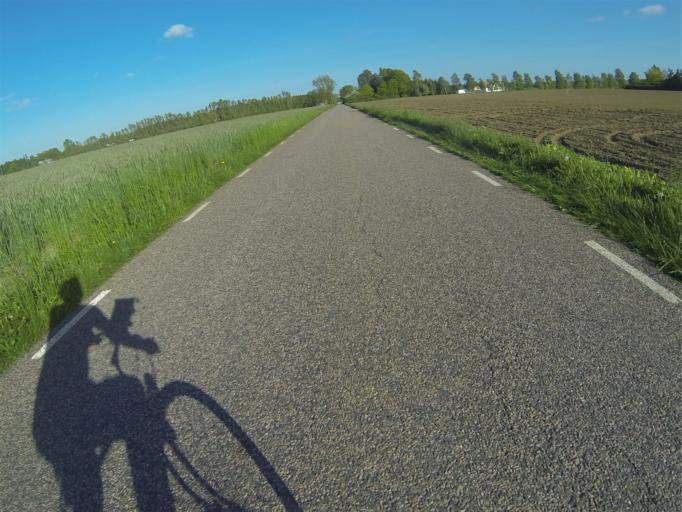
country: SE
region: Skane
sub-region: Eslovs Kommun
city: Eslov
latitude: 55.7326
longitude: 13.3754
